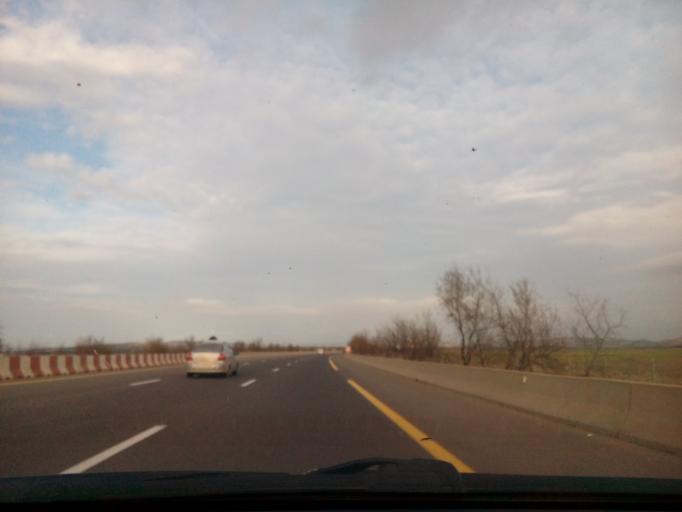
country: DZ
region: Mostaganem
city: Mostaganem
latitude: 35.6828
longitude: 0.1562
